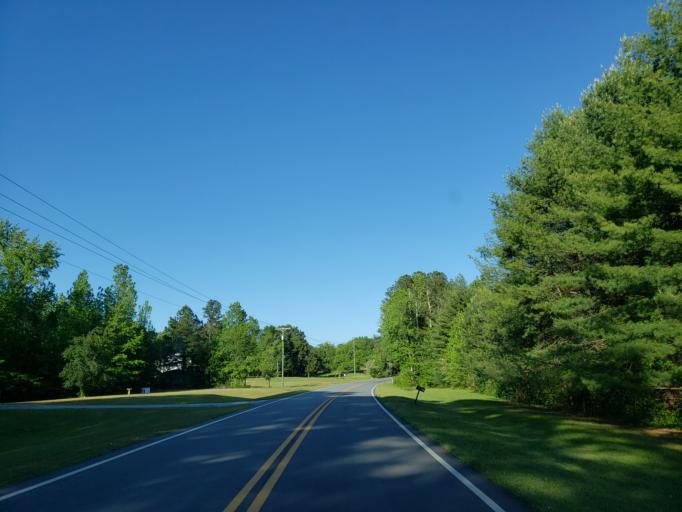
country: US
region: Georgia
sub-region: Haralson County
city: Buchanan
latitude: 33.8099
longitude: -85.2313
